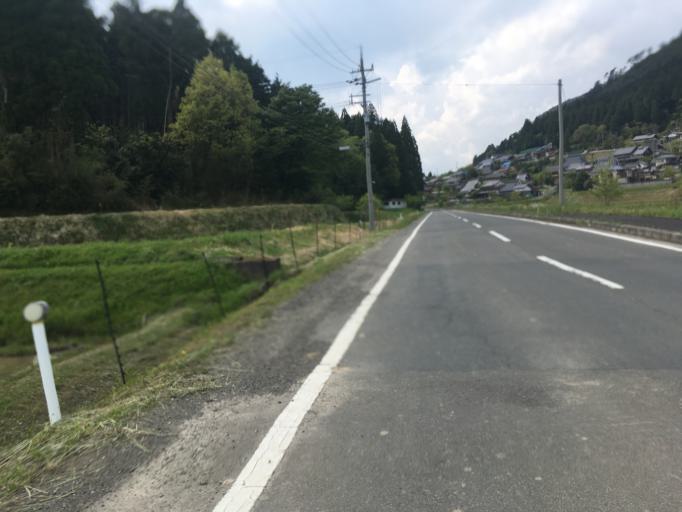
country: JP
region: Kyoto
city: Kameoka
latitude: 35.1070
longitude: 135.5818
